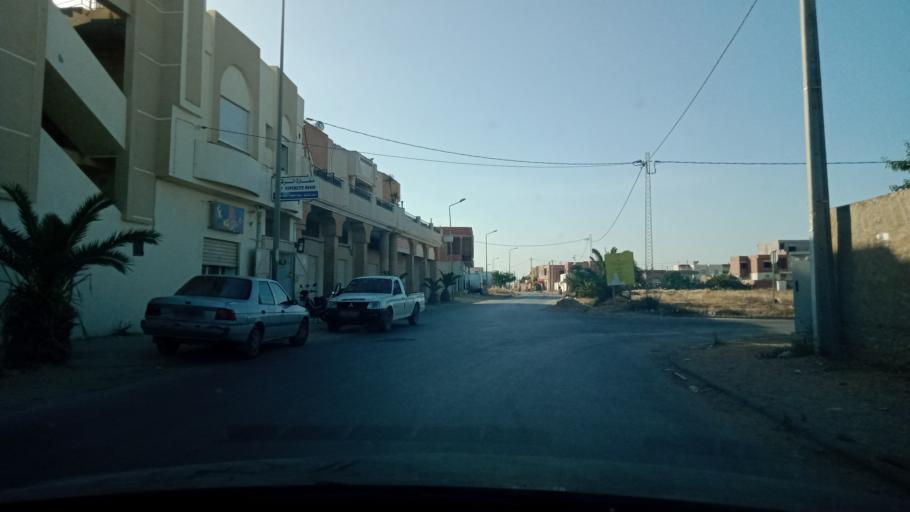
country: TN
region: Safaqis
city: Al Qarmadah
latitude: 34.8208
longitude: 10.7413
